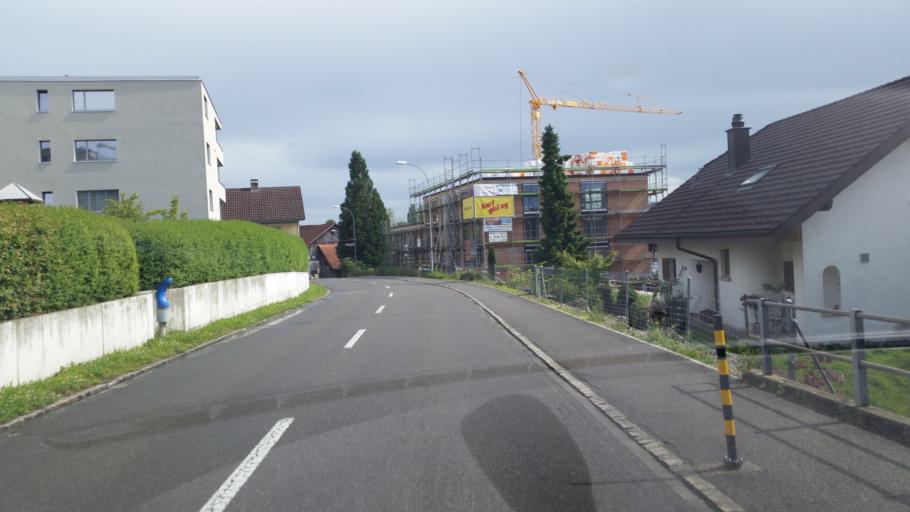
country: CH
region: Aargau
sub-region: Bezirk Lenzburg
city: Seengen
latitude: 47.3244
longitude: 8.2071
